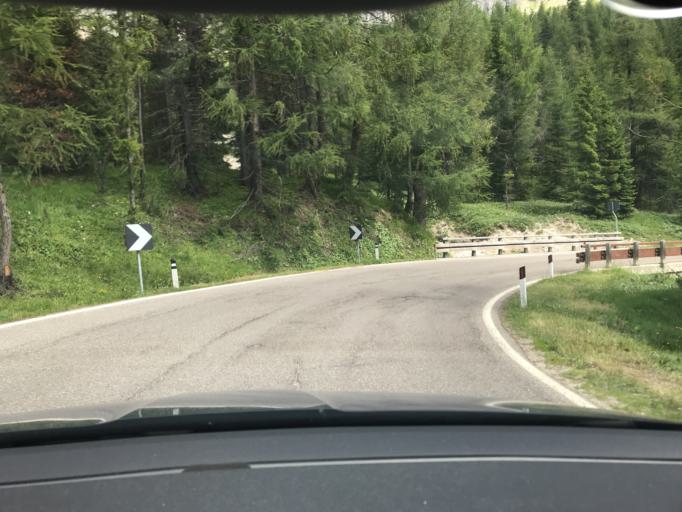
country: IT
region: Veneto
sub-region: Provincia di Belluno
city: Colle Santa Lucia
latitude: 46.5194
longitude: 12.0313
